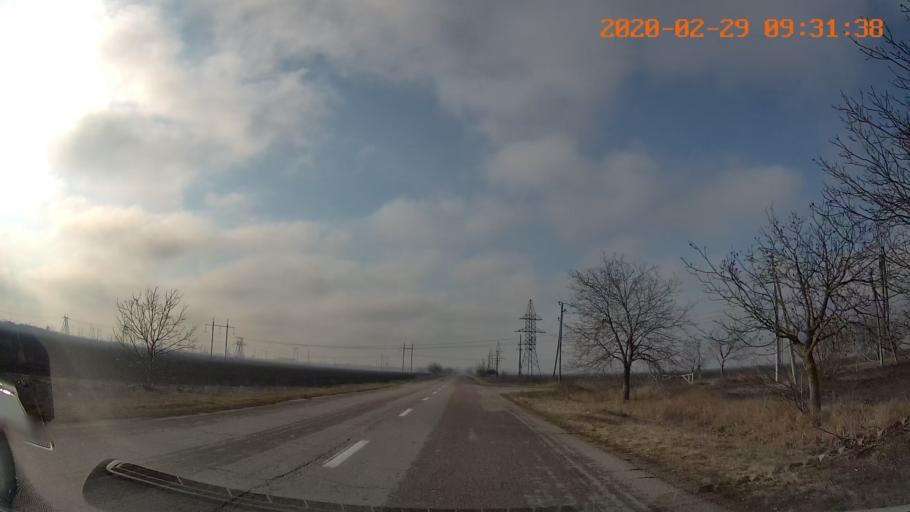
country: MD
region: Telenesti
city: Dnestrovsc
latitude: 46.6501
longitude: 29.9101
